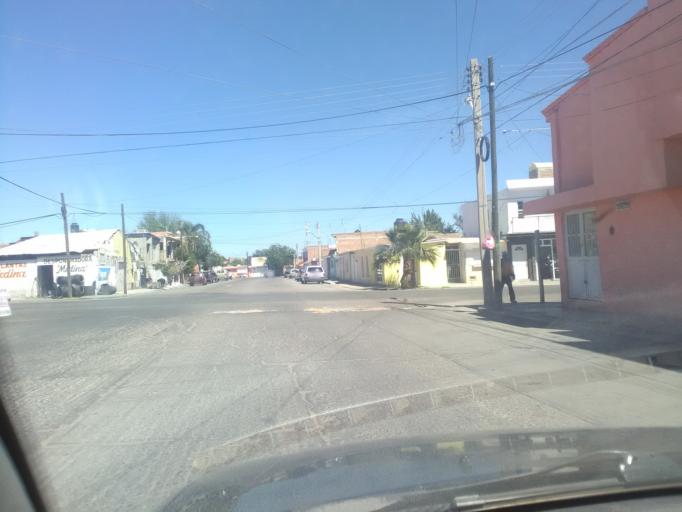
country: MX
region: Durango
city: Victoria de Durango
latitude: 24.0157
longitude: -104.6575
